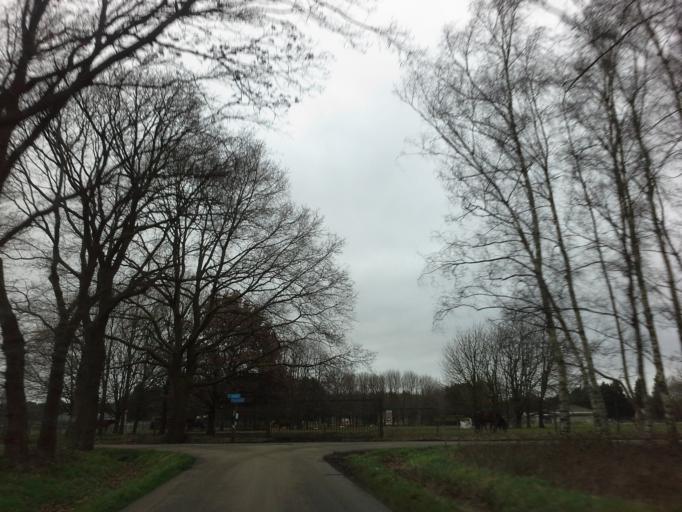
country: BE
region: Flanders
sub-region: Provincie Antwerpen
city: Meerhout
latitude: 51.1211
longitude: 5.0654
